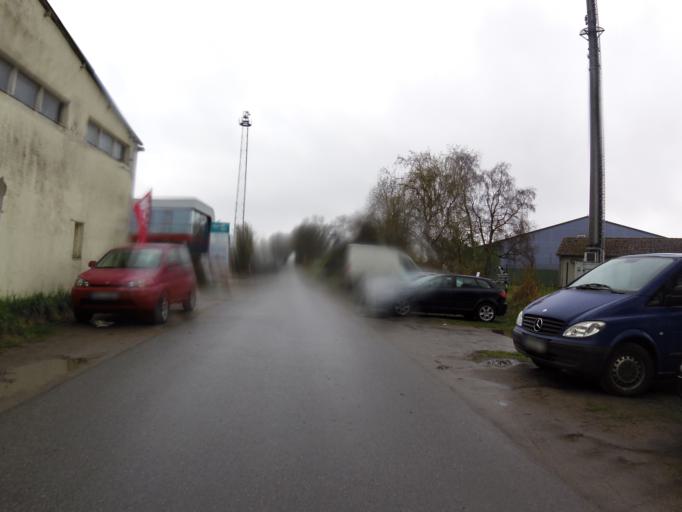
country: DE
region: Mecklenburg-Vorpommern
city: Zingst
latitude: 54.4332
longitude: 12.7035
